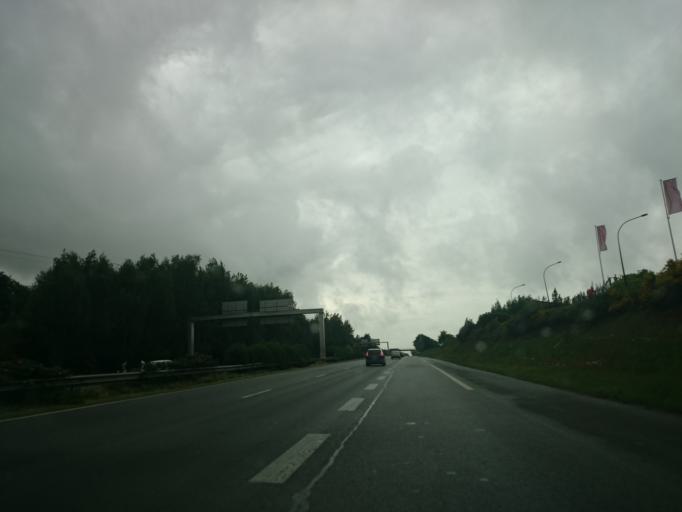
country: FR
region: Brittany
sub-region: Departement d'Ille-et-Vilaine
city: Chantepie
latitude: 48.0992
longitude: -1.6144
